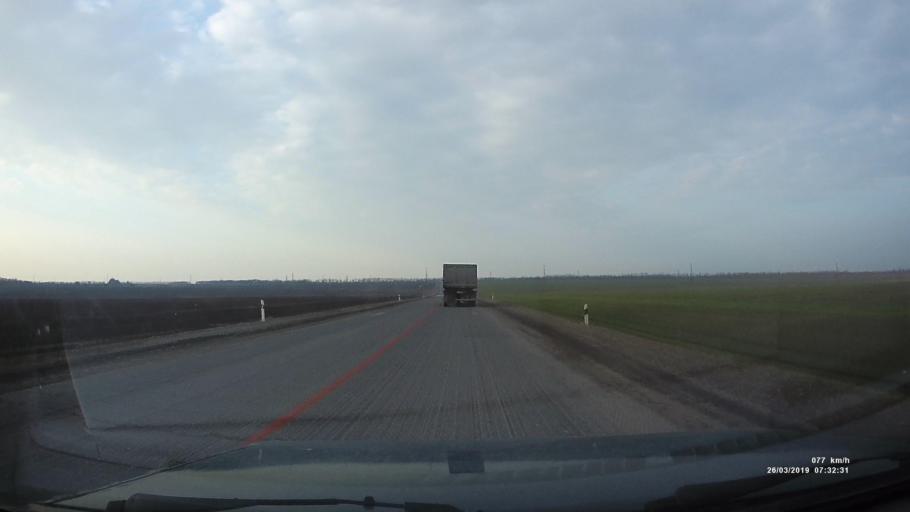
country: RU
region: Rostov
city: Novobessergenovka
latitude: 47.2248
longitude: 38.7771
